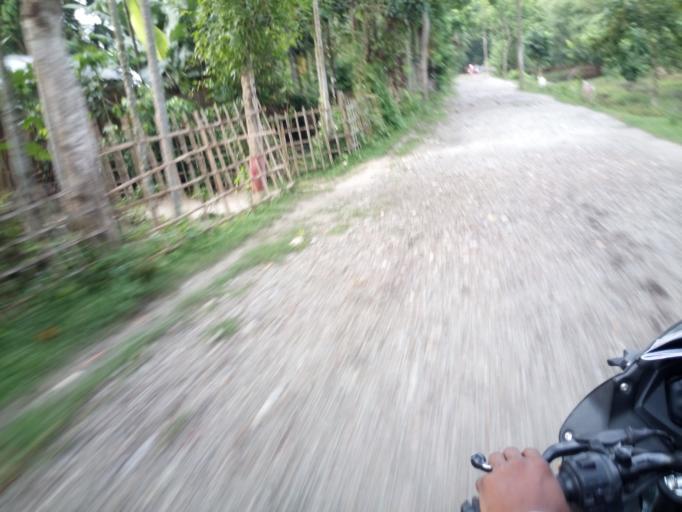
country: IN
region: Assam
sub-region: Darrang
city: Kharupatia
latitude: 26.6267
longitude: 92.2905
